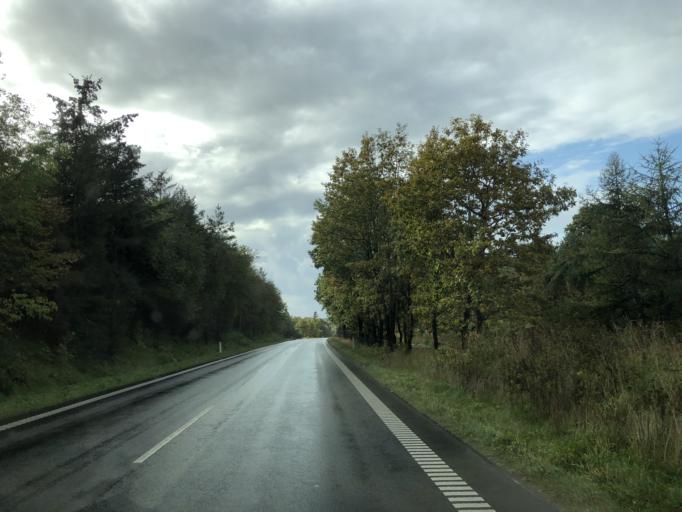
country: DK
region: North Denmark
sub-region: Vesthimmerland Kommune
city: Alestrup
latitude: 56.6127
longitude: 9.4433
